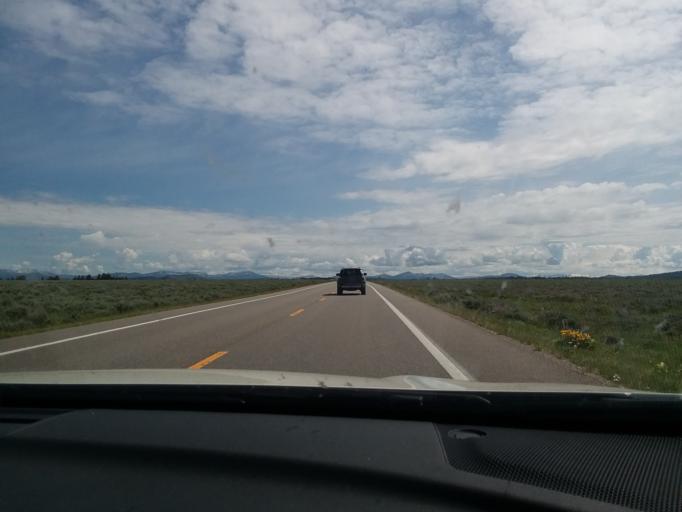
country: US
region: Wyoming
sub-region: Teton County
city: Jackson
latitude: 43.7307
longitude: -110.6466
